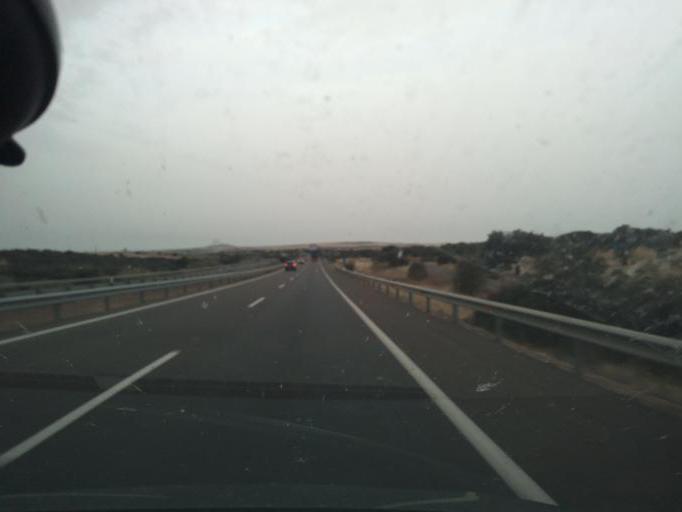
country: ES
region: Extremadura
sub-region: Provincia de Badajoz
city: Trujillanos
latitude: 38.9524
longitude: -6.2354
